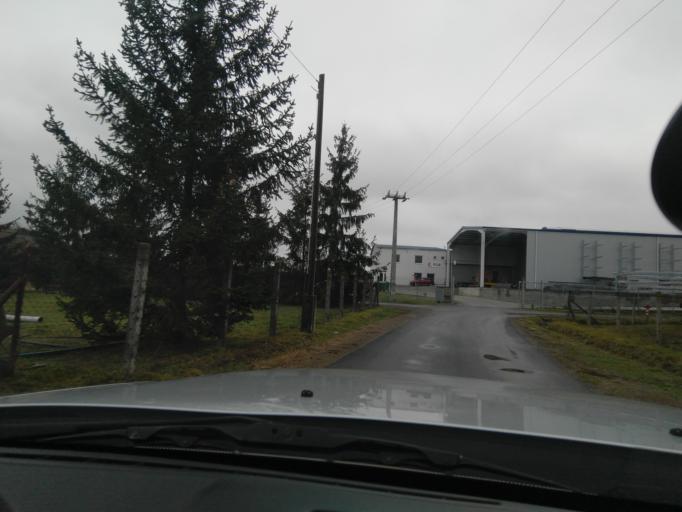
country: HU
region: Nograd
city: Matraterenye
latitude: 48.0301
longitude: 19.9530
